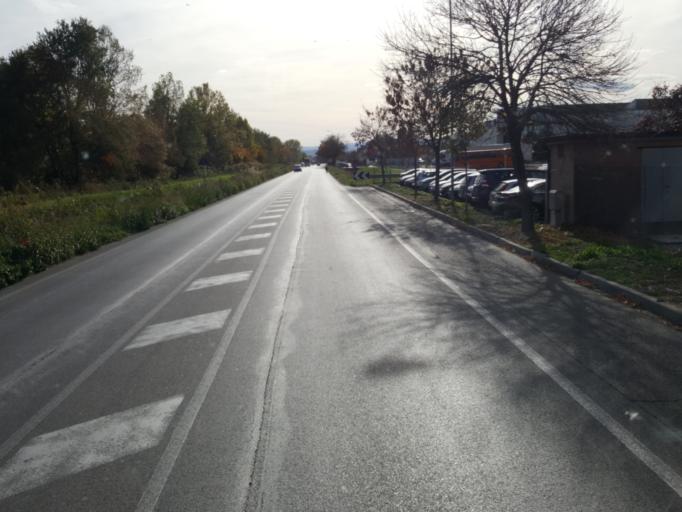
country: IT
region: Emilia-Romagna
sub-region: Provincia di Ravenna
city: Faenza
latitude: 44.3174
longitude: 11.9022
